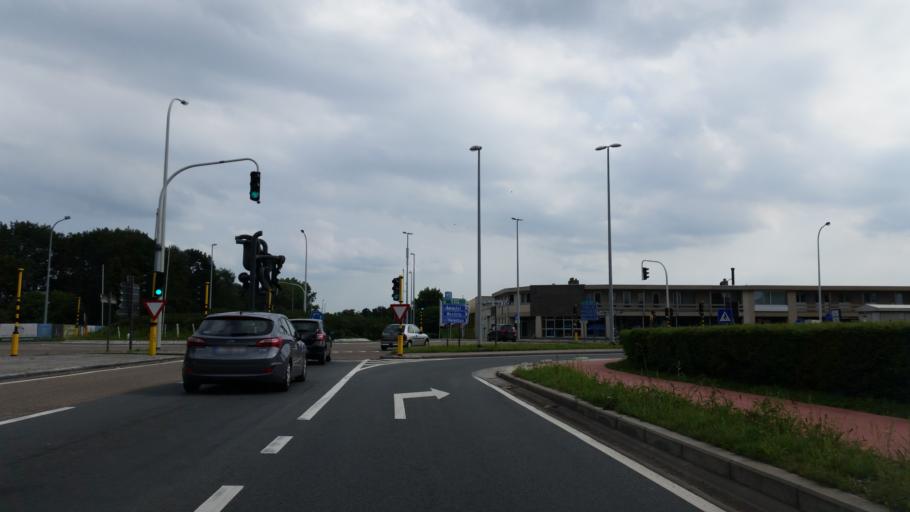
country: BE
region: Flanders
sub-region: Provincie Antwerpen
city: Geel
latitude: 51.1532
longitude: 4.9742
